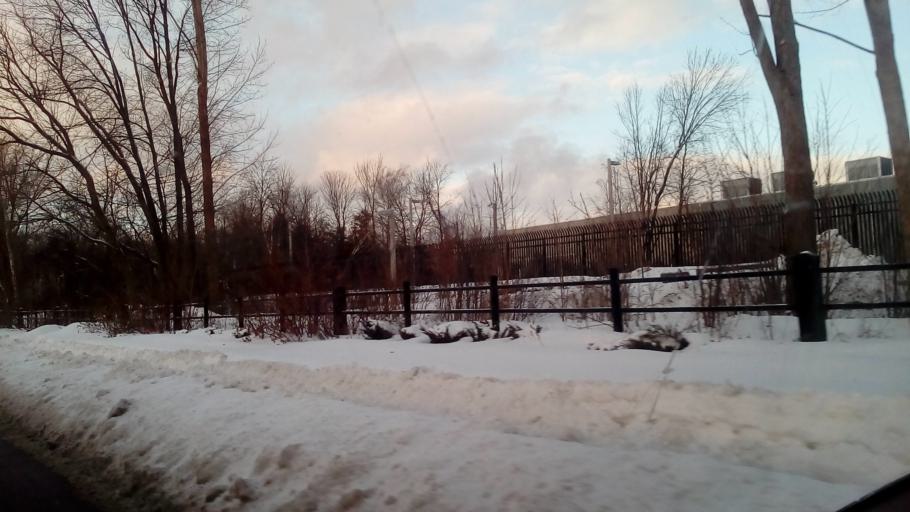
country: CA
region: Ontario
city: Ottawa
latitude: 45.4350
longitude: -75.6189
